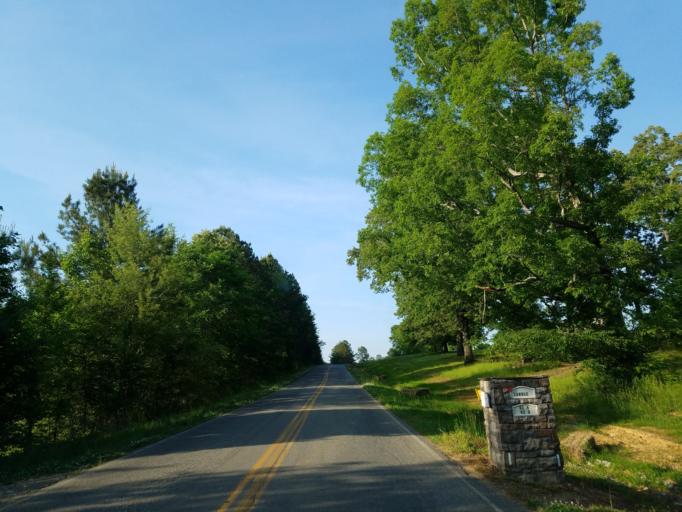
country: US
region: Georgia
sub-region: Floyd County
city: Shannon
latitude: 34.4823
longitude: -85.1362
